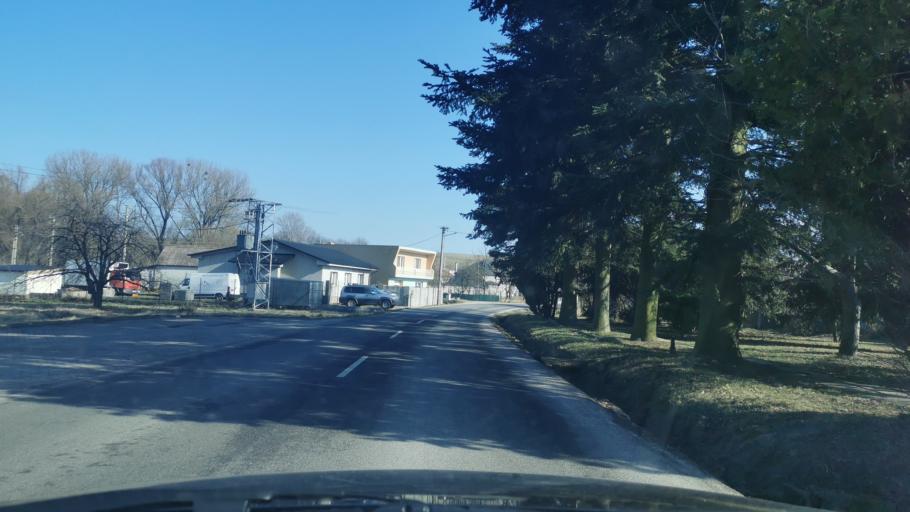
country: SK
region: Trnavsky
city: Gbely
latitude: 48.7144
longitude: 17.1757
